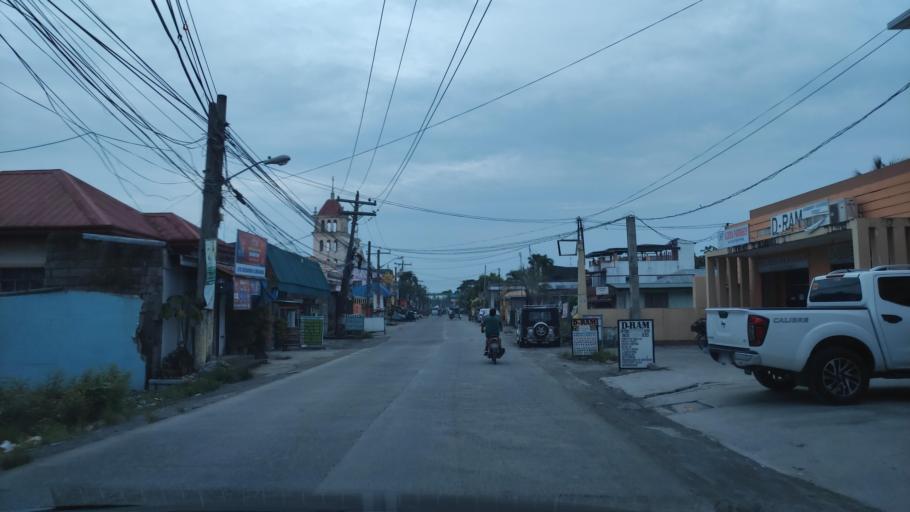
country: PH
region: Central Luzon
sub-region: Province of Nueva Ecija
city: San Anton
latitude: 15.3405
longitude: 120.9130
